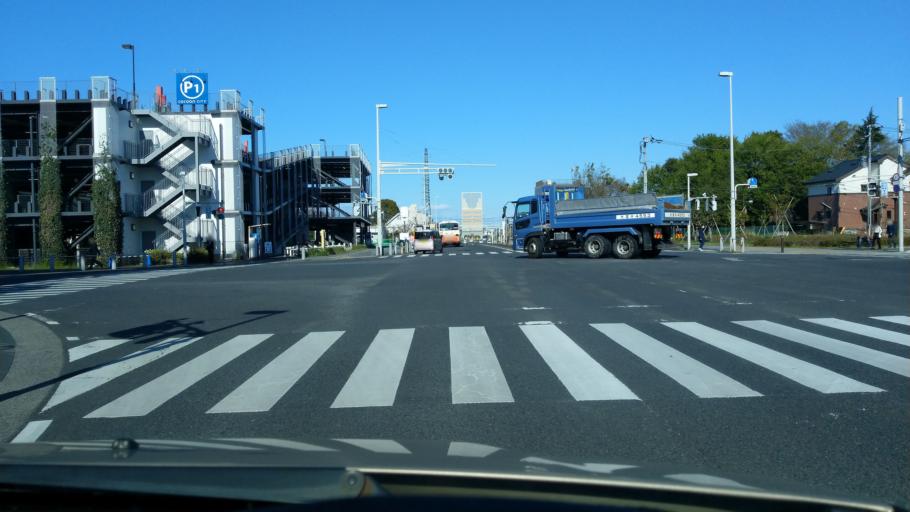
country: JP
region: Saitama
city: Yono
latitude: 35.8947
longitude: 139.6388
